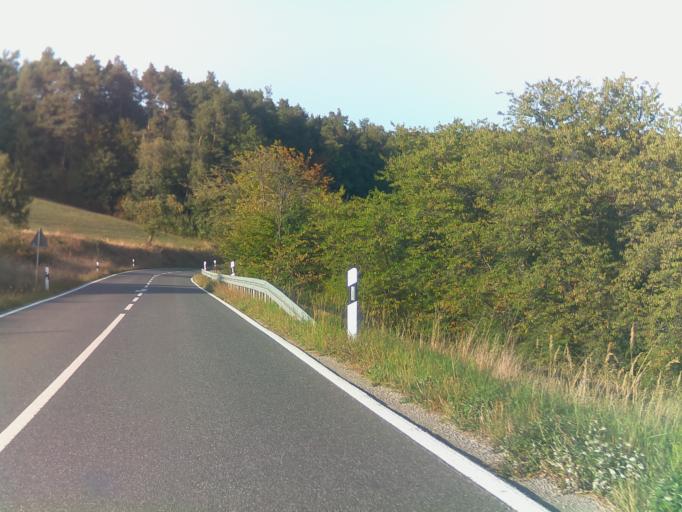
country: DE
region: Bavaria
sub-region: Regierungsbezirk Unterfranken
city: Aura im Sinngrund
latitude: 50.1755
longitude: 9.5555
